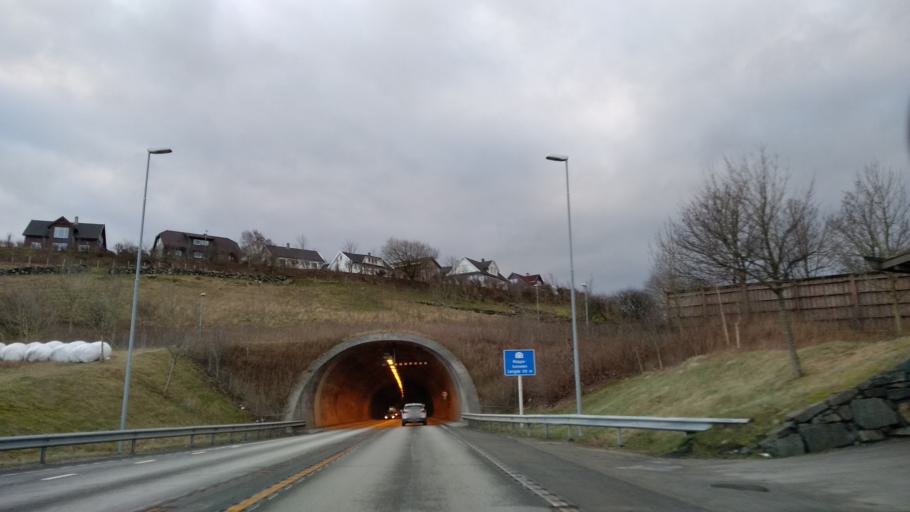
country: NO
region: Rogaland
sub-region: Klepp
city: Kleppe
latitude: 58.7783
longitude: 5.6230
